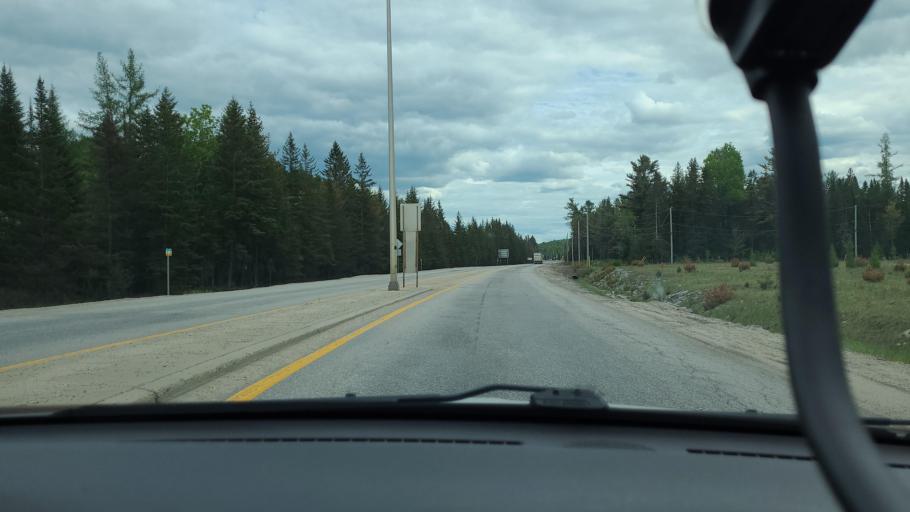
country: CA
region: Quebec
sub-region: Laurentides
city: Riviere-Rouge
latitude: 46.3886
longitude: -74.8599
